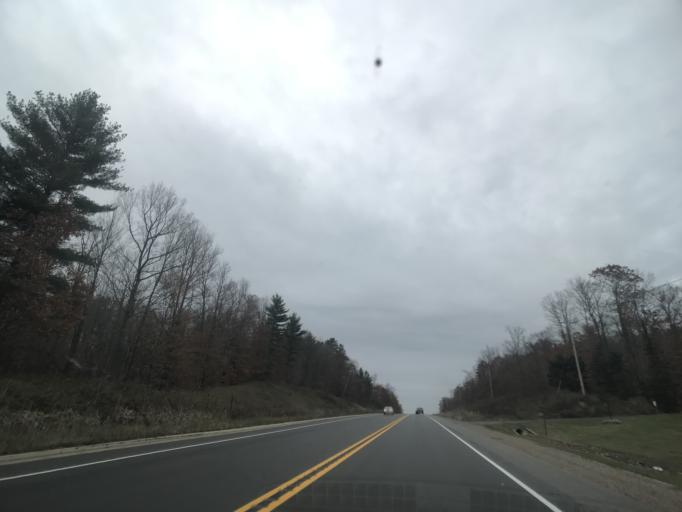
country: US
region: Wisconsin
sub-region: Menominee County
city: Legend Lake
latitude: 45.2444
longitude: -88.5152
